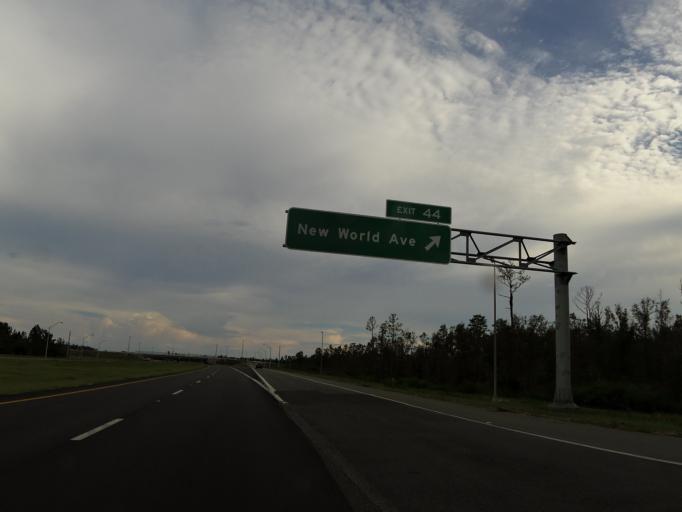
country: US
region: Florida
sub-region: Duval County
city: Baldwin
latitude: 30.2822
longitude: -81.8784
